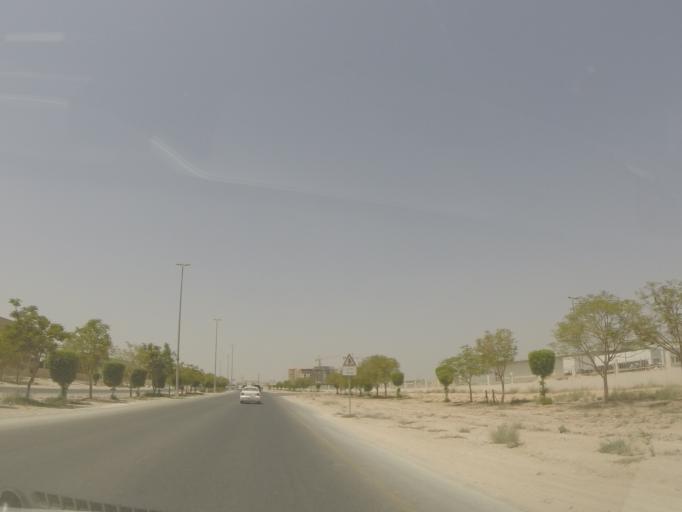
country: AE
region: Dubai
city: Dubai
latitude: 24.9867
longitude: 55.1892
